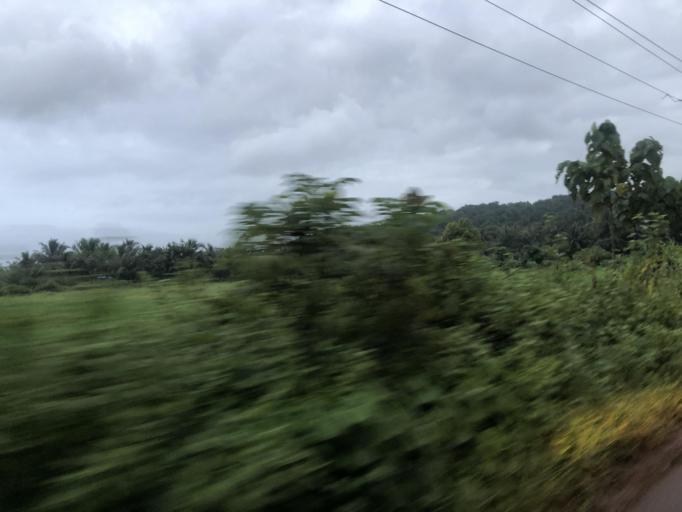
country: IN
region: Goa
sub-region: North Goa
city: Serula
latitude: 15.5523
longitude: 73.8193
